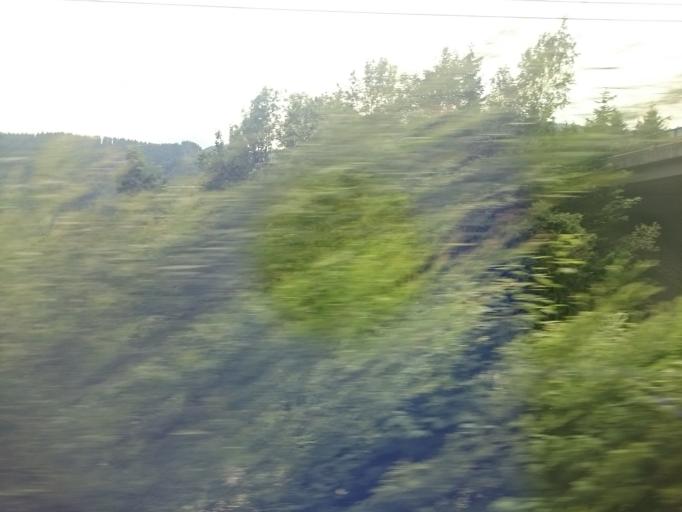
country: AT
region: Tyrol
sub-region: Politischer Bezirk Kufstein
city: Worgl
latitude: 47.4818
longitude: 12.0281
